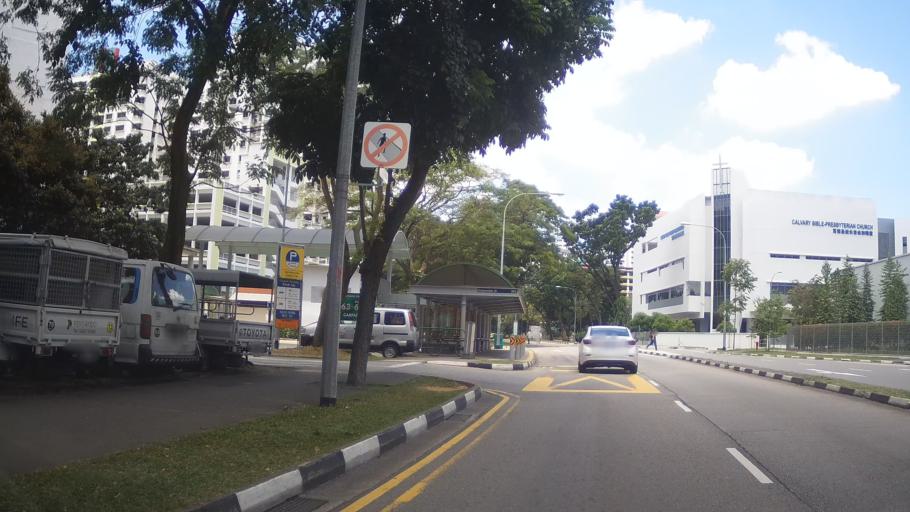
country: SG
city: Singapore
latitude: 1.3321
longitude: 103.7234
